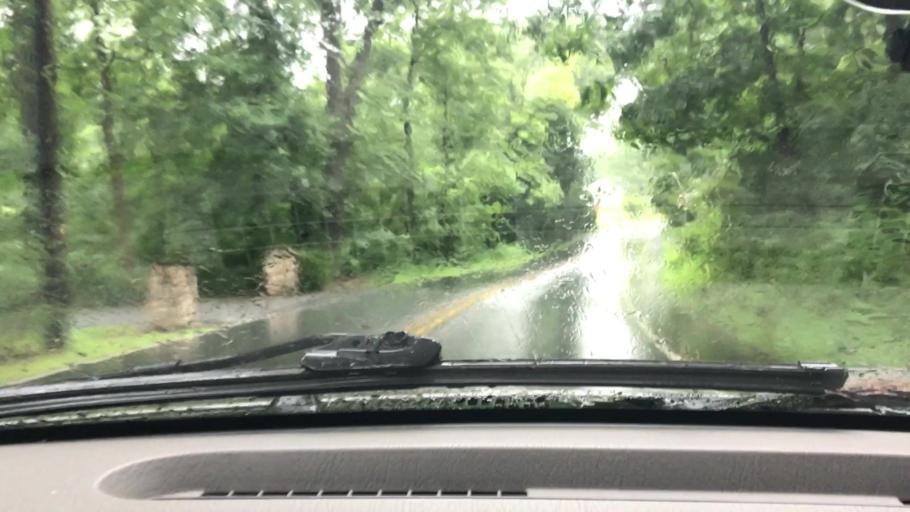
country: US
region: Pennsylvania
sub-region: Lancaster County
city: Elizabethtown
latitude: 40.1496
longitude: -76.6305
